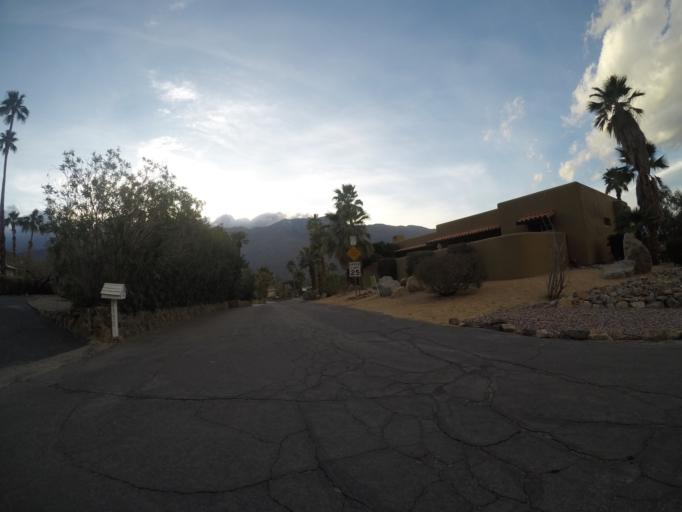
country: US
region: California
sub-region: Riverside County
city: Palm Springs
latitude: 33.7905
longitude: -116.5148
